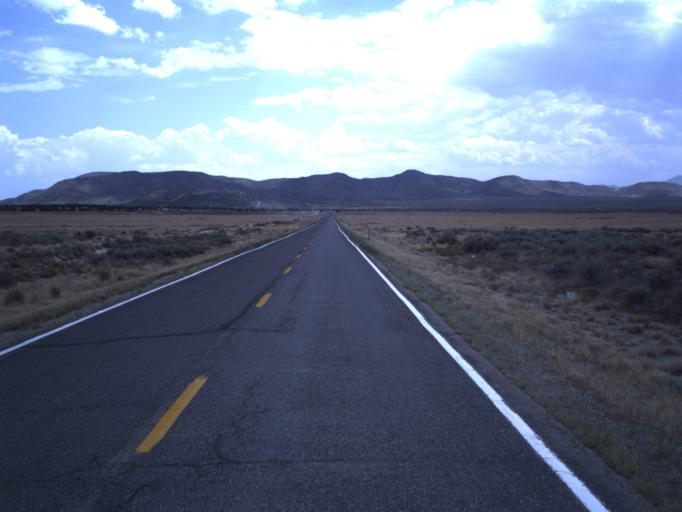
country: US
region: Utah
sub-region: Utah County
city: Eagle Mountain
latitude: 40.2474
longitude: -112.2139
